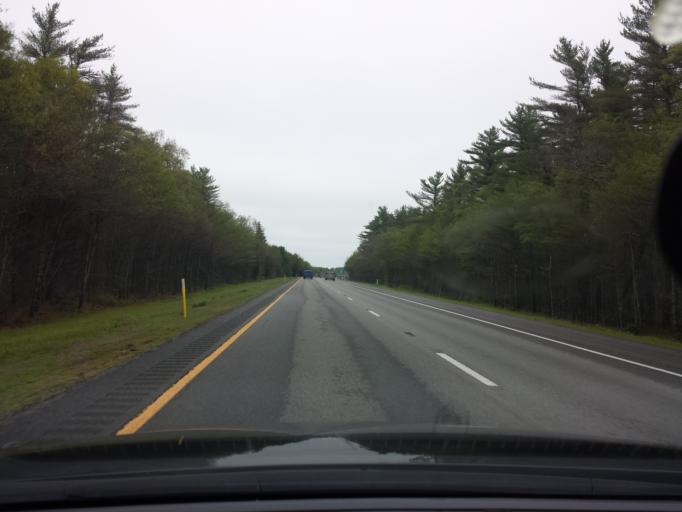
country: US
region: Massachusetts
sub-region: Plymouth County
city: Marion Center
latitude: 41.7184
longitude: -70.7823
